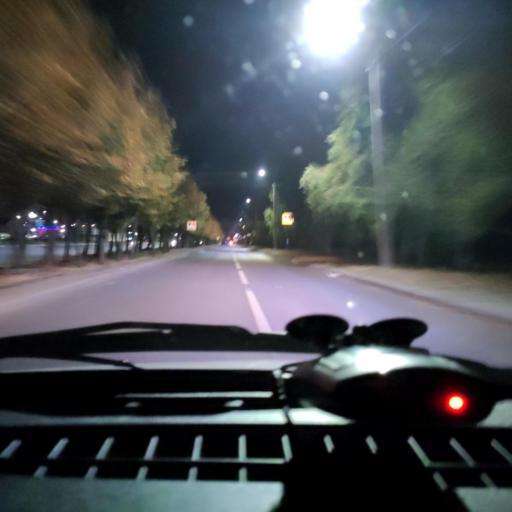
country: RU
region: Voronezj
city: Podgornoye
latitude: 51.7085
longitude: 39.1629
